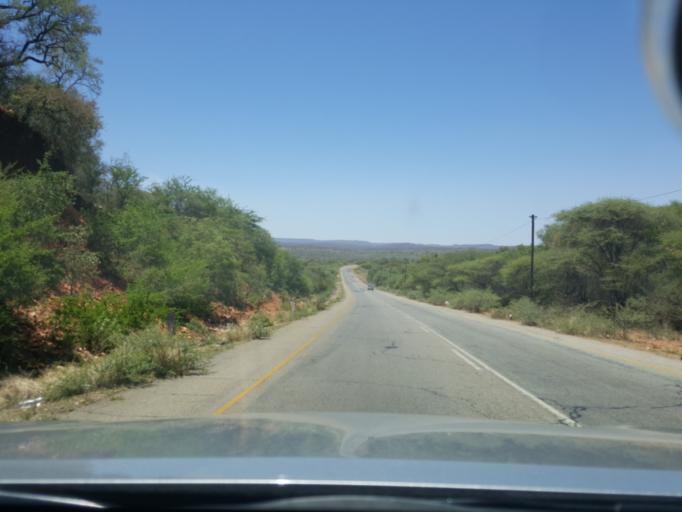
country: ZA
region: North-West
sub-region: Ngaka Modiri Molema District Municipality
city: Zeerust
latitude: -25.3209
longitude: 25.9374
